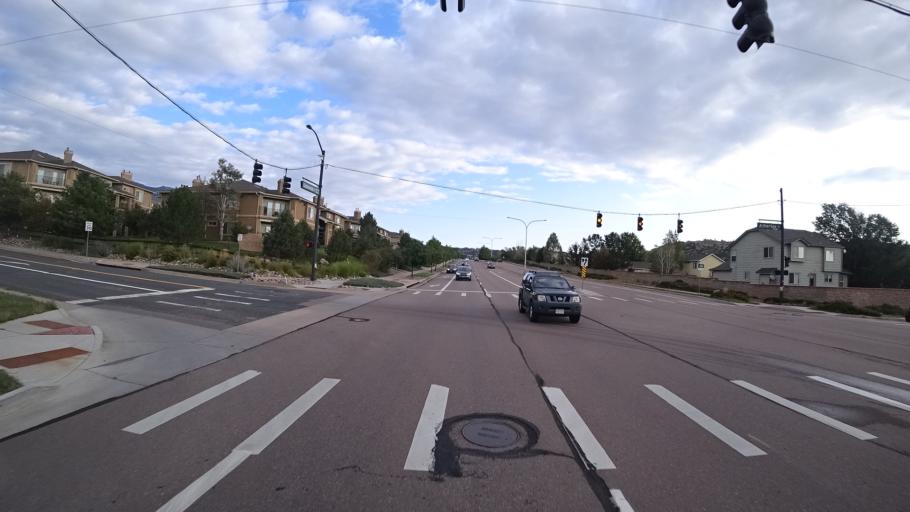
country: US
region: Colorado
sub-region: El Paso County
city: Manitou Springs
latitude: 38.9159
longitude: -104.8637
